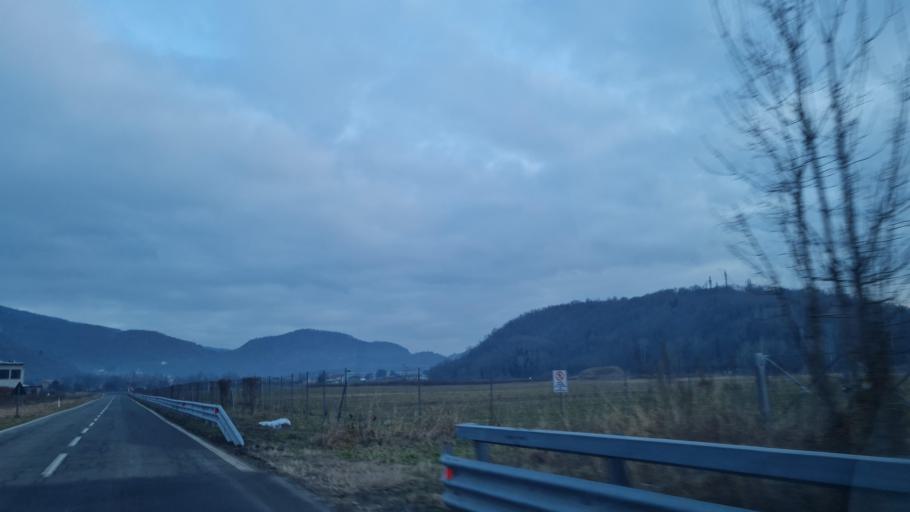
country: IT
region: Piedmont
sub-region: Provincia di Torino
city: Quassolo
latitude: 45.5205
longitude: 7.8416
